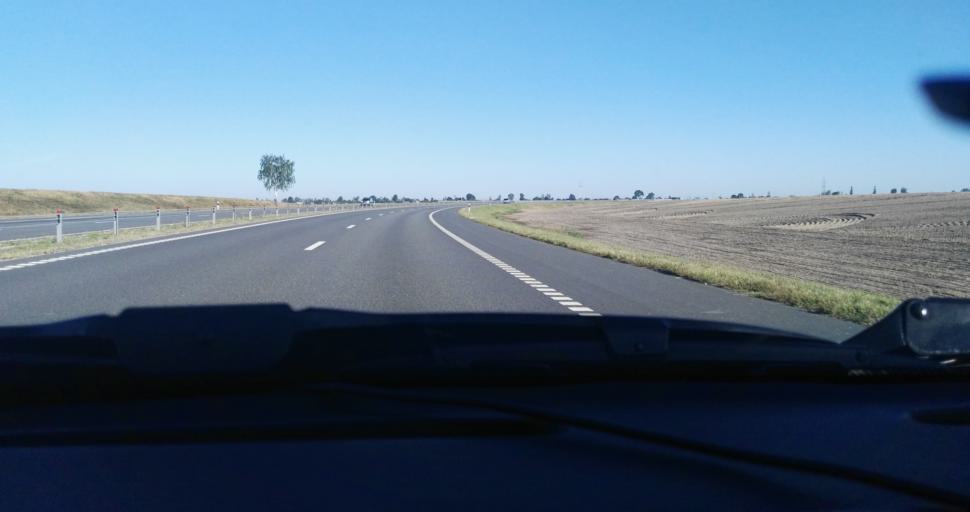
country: BY
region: Gomel
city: Buda-Kashalyova
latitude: 52.5089
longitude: 30.6332
